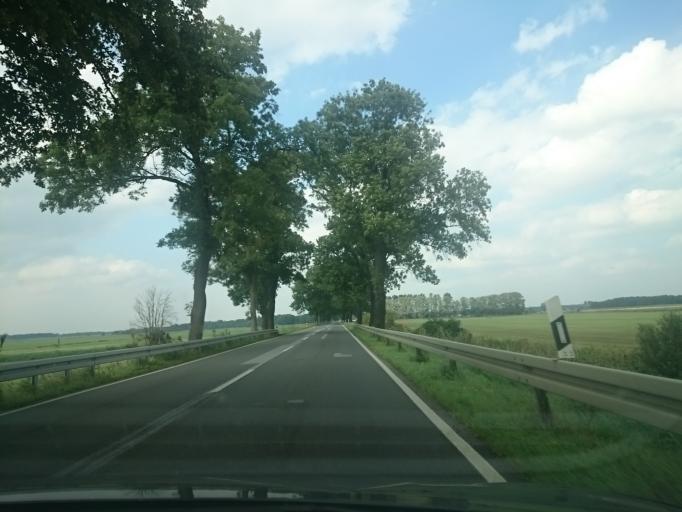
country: DE
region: Mecklenburg-Vorpommern
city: Ferdinandshof
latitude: 53.6776
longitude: 13.8848
